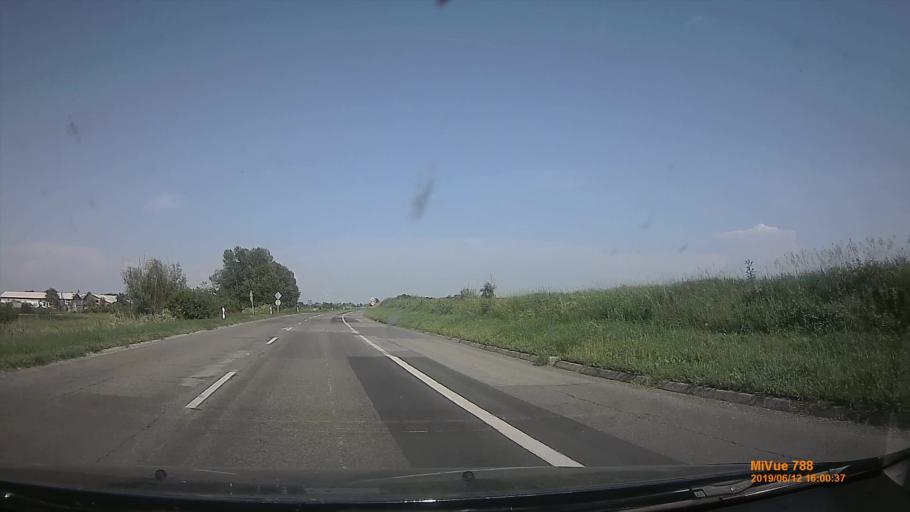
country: RO
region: Arad
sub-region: Comuna Nadlac
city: Nadlac
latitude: 46.1685
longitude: 20.6828
